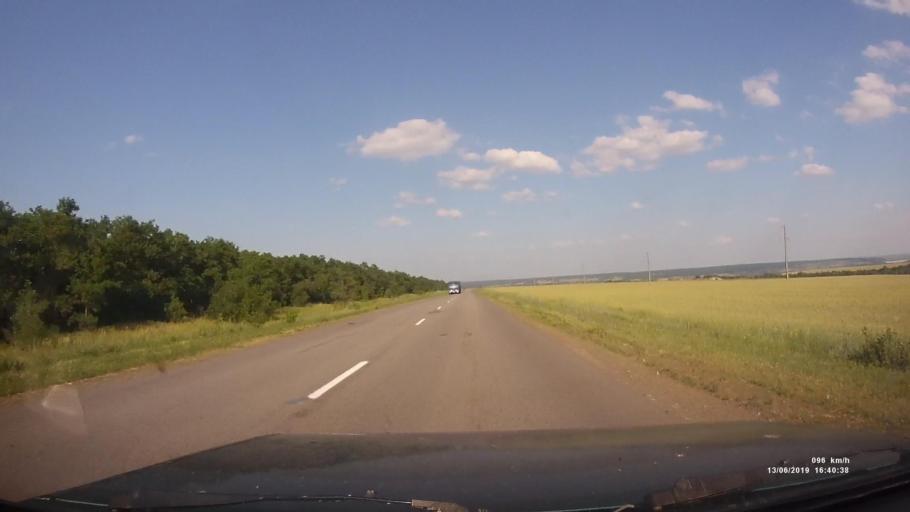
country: RU
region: Rostov
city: Kazanskaya
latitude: 49.9330
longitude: 41.3658
